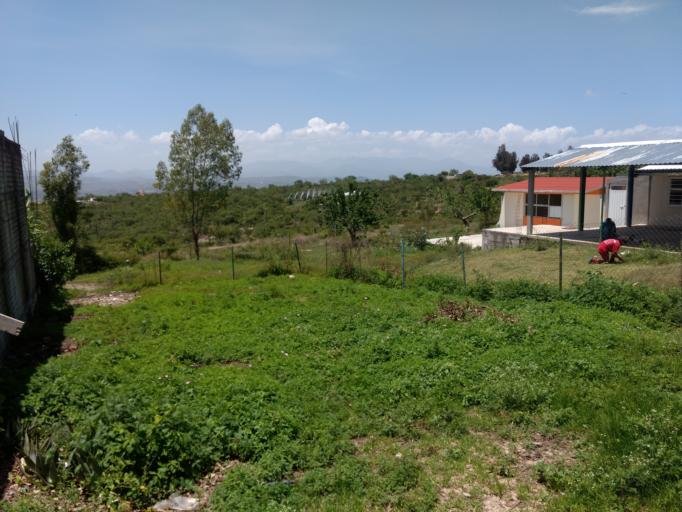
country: MX
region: Oaxaca
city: San Jeronimo Silacayoapilla
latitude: 17.8172
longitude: -97.8131
